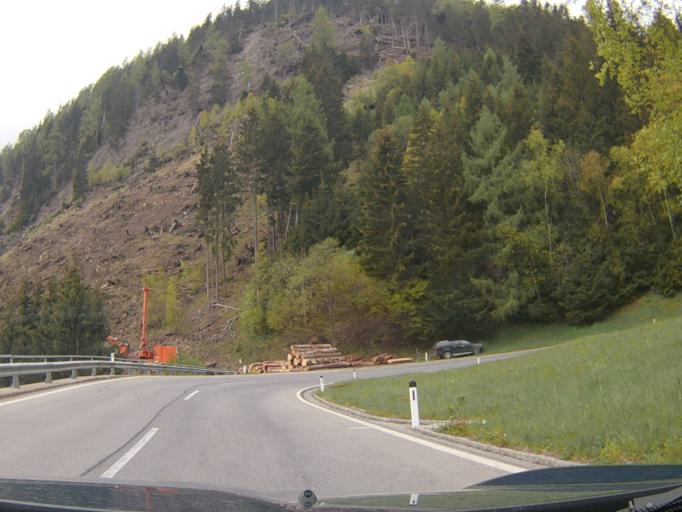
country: AT
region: Carinthia
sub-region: Politischer Bezirk Spittal an der Drau
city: Obervellach
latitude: 46.9674
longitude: 13.1820
